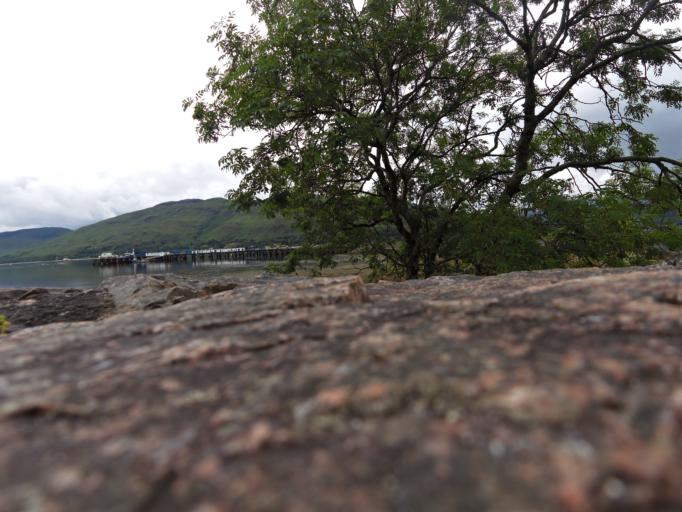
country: GB
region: Scotland
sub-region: Highland
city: Fort William
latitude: 56.8215
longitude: -5.1081
